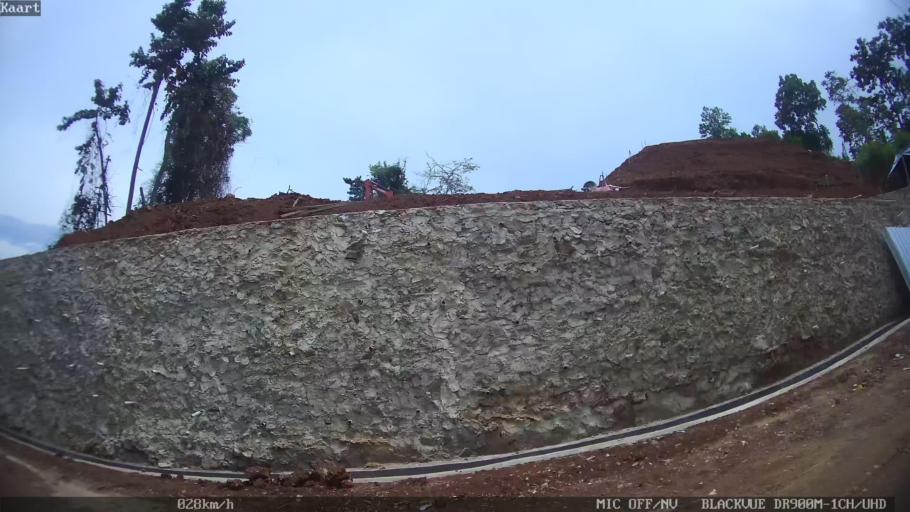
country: ID
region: Lampung
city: Bandarlampung
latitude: -5.4373
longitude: 105.2469
